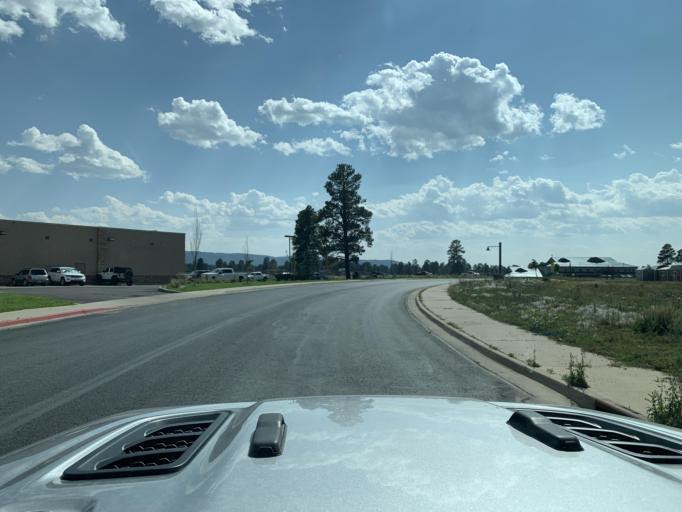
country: US
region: Colorado
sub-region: Archuleta County
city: Pagosa Springs
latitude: 37.2627
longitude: -107.0590
